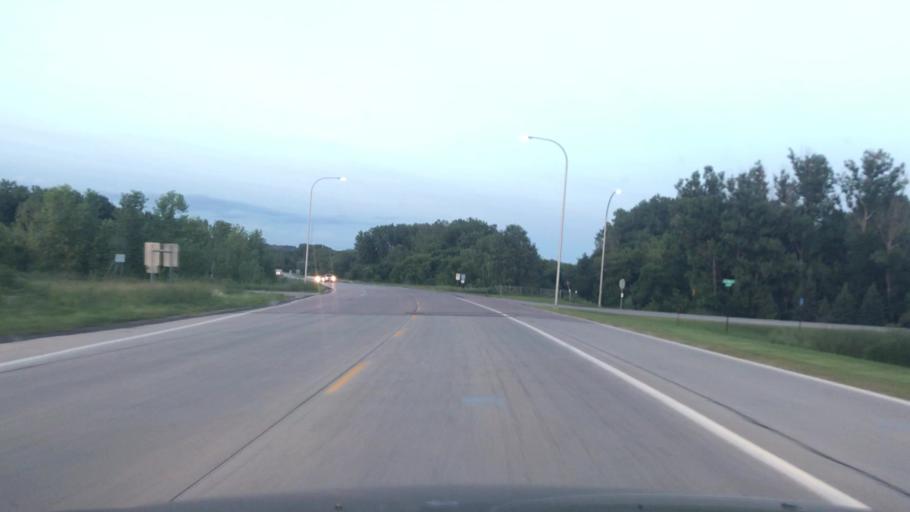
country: US
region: Minnesota
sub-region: Redwood County
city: Redwood Falls
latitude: 44.5401
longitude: -95.0072
